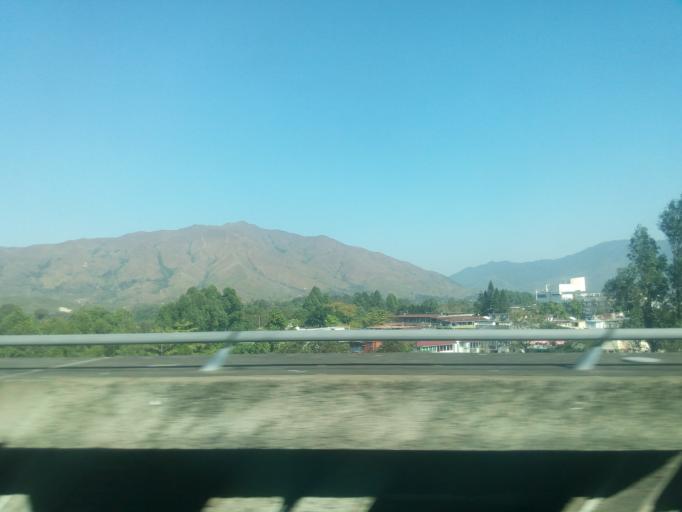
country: HK
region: Yuen Long
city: Yuen Long Kau Hui
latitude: 22.4401
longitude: 114.0600
